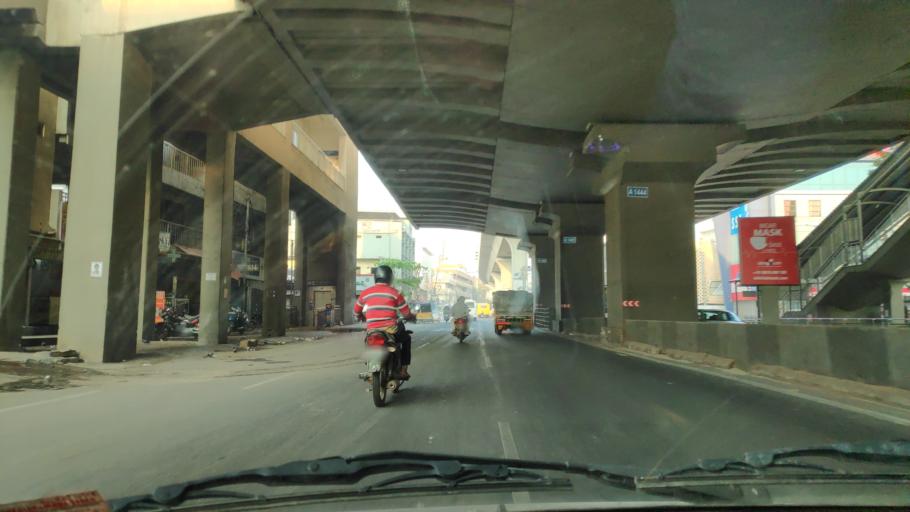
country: IN
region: Telangana
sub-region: Rangareddi
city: Gaddi Annaram
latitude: 17.3735
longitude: 78.5029
